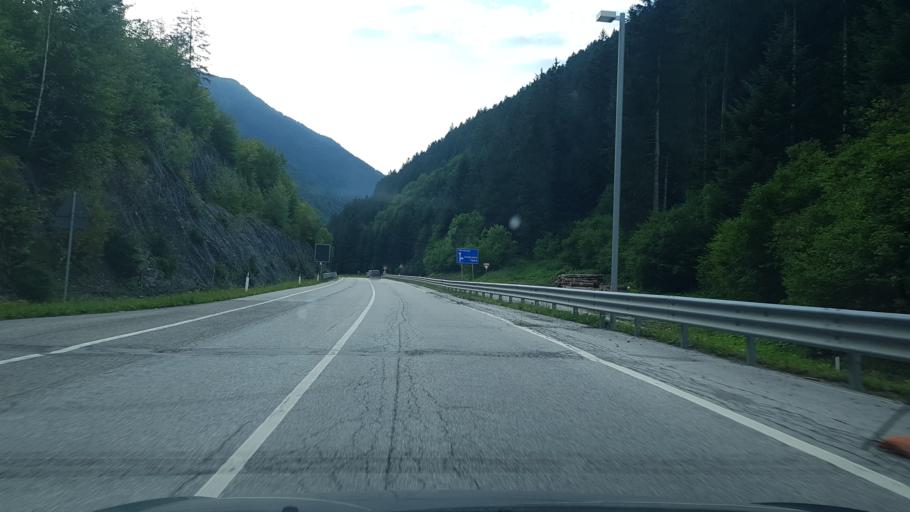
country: IT
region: Friuli Venezia Giulia
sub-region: Provincia di Udine
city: Rigolato
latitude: 46.5682
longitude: 12.8295
